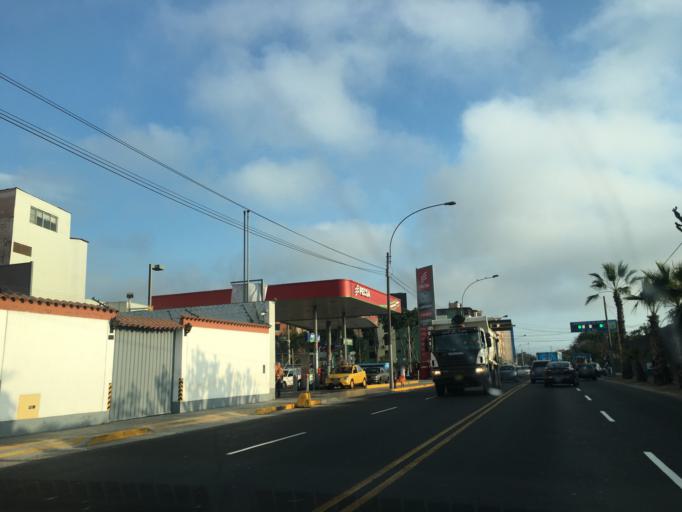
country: PE
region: Callao
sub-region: Callao
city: Callao
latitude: -12.0739
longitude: -77.0836
